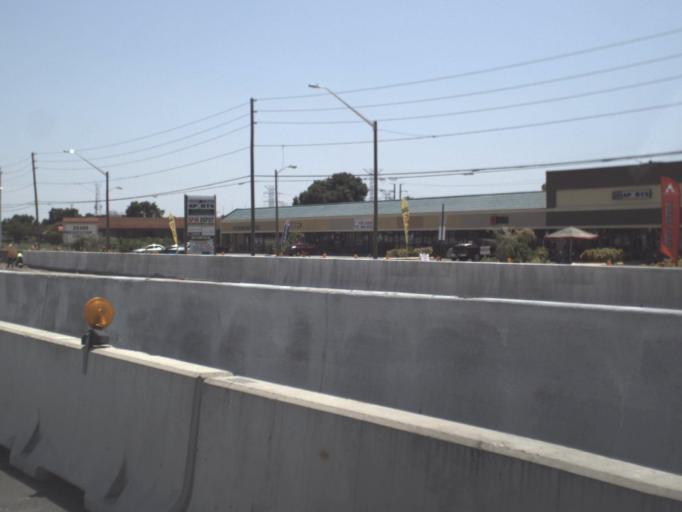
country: US
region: Florida
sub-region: Pinellas County
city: Safety Harbor
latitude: 28.0067
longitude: -82.7298
